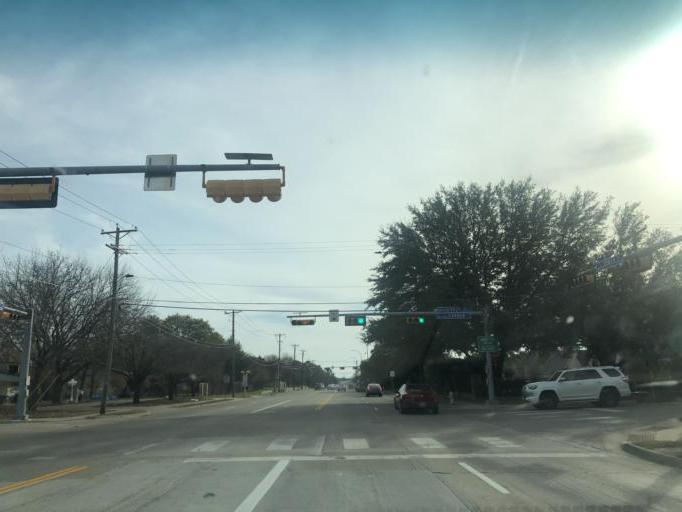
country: US
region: Texas
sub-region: Tarrant County
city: Dalworthington Gardens
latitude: 32.6865
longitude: -97.1495
